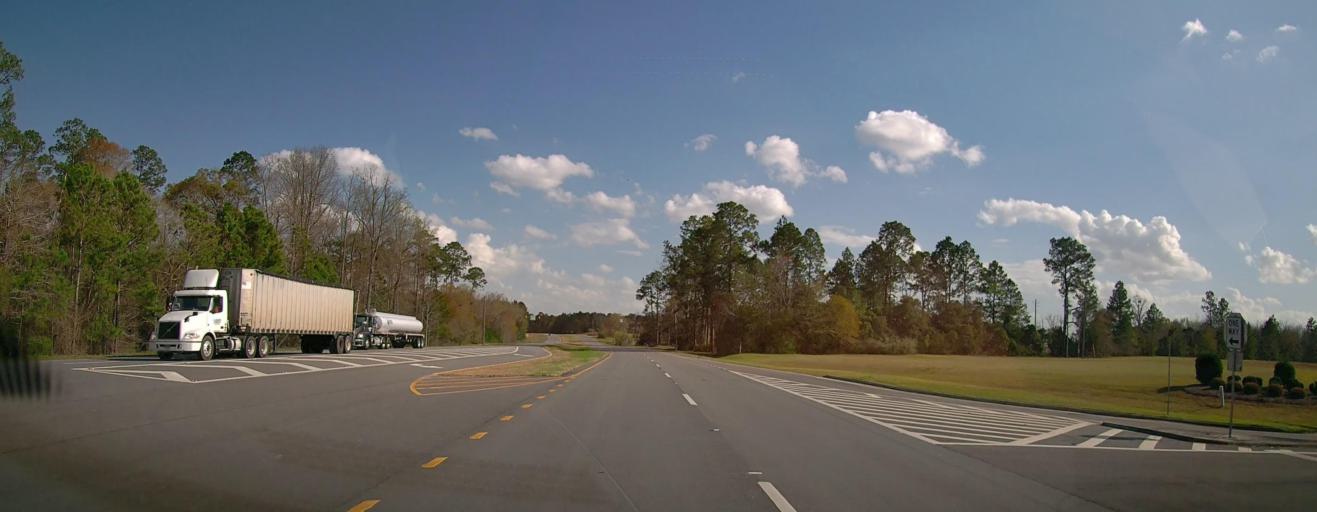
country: US
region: Georgia
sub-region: Telfair County
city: McRae
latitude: 32.0497
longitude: -82.8604
